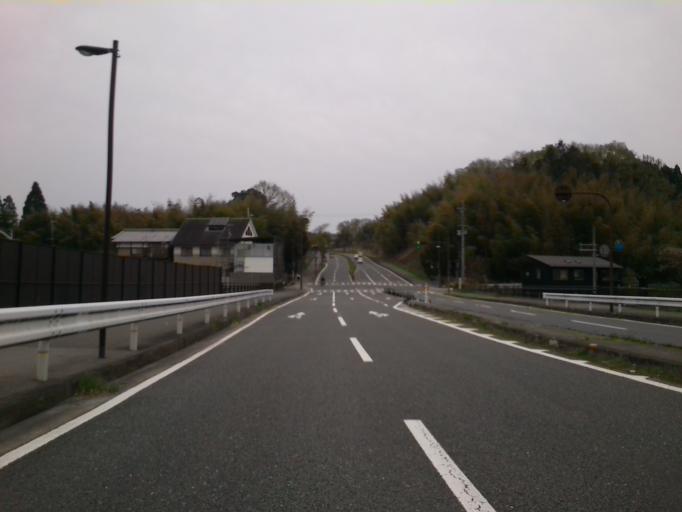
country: JP
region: Kyoto
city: Tanabe
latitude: 34.8081
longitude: 135.7686
